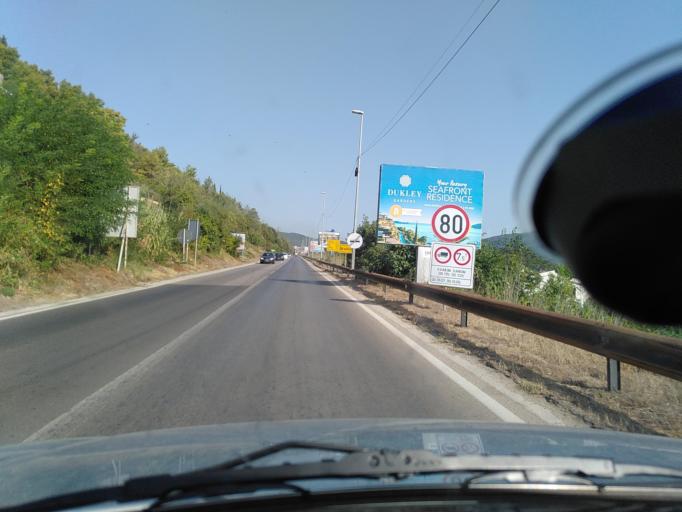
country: ME
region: Ulcinj
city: Ulcinj
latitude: 41.9386
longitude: 19.2168
